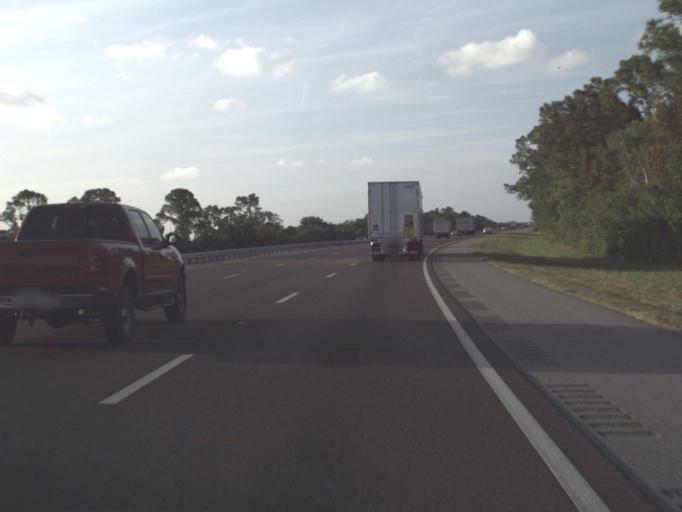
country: US
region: Florida
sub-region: Brevard County
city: Port Saint John
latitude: 28.5193
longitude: -80.8515
